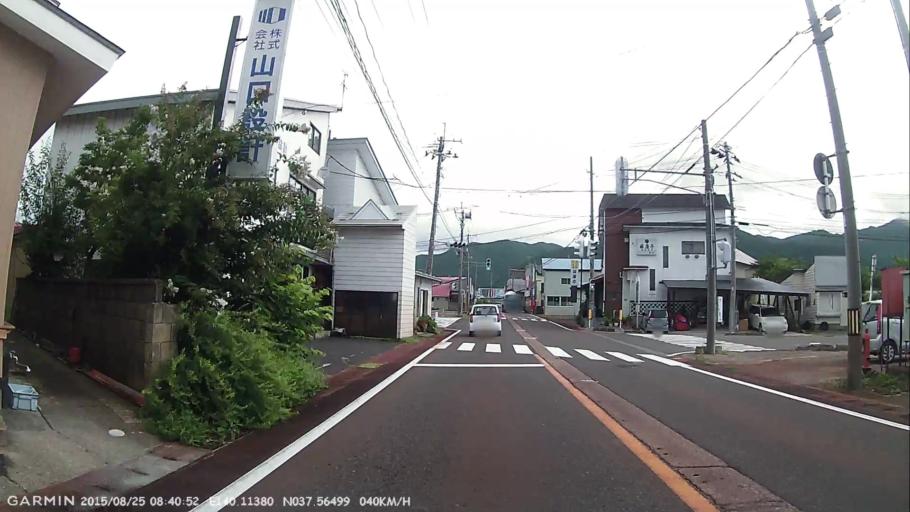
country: JP
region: Fukushima
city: Inawashiro
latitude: 37.5651
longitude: 140.1140
